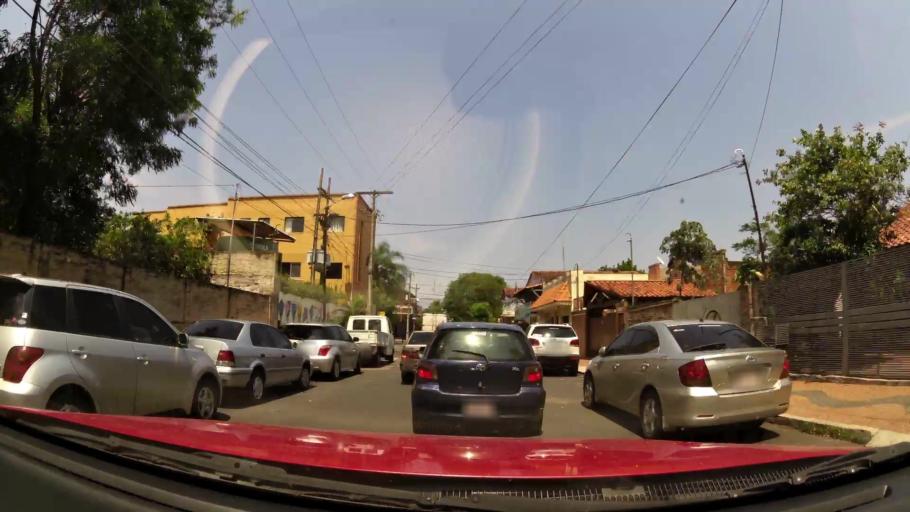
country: PY
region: Asuncion
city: Asuncion
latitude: -25.2938
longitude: -57.6423
